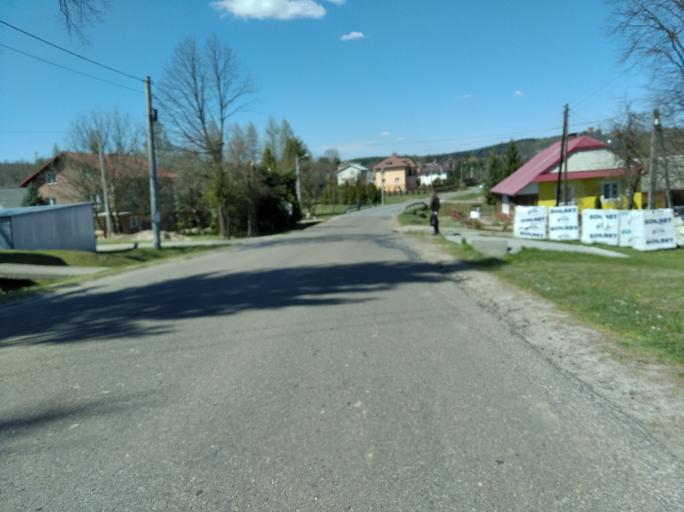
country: PL
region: Subcarpathian Voivodeship
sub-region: Powiat brzozowski
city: Dydnia
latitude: 49.6916
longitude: 22.1548
